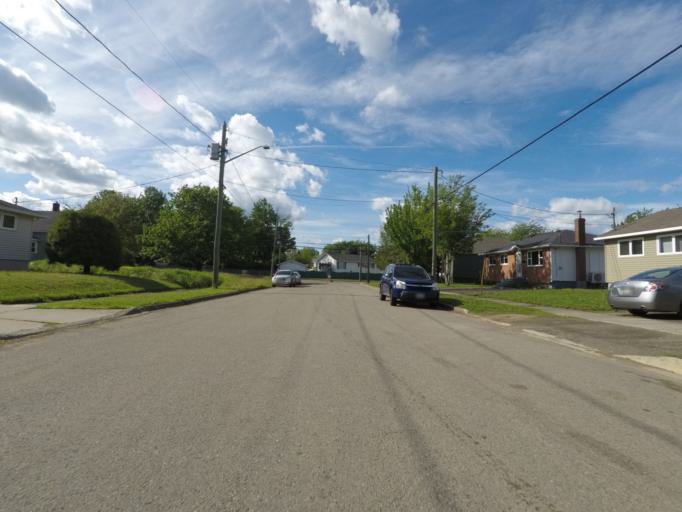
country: CA
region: New Brunswick
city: Moncton
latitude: 46.1034
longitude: -64.8246
